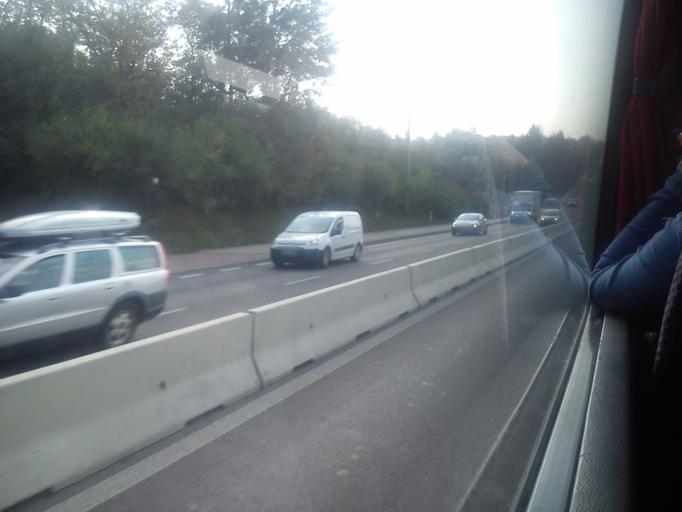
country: PL
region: Subcarpathian Voivodeship
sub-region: Powiat lancucki
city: Lancut
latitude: 50.0607
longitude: 22.2154
